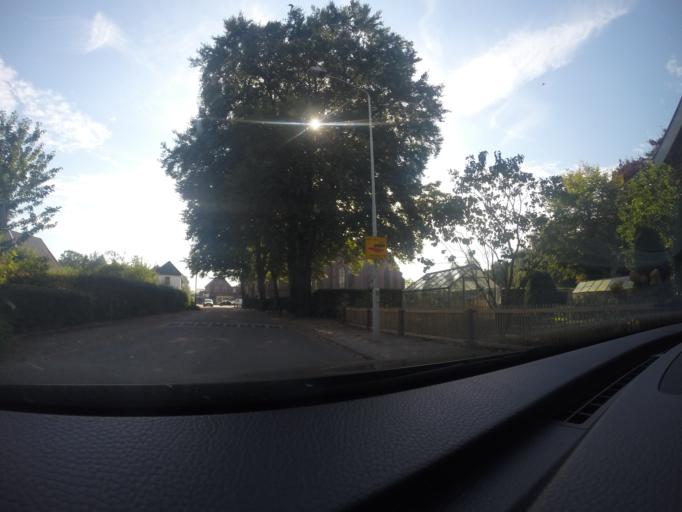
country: NL
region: Gelderland
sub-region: Gemeente Doetinchem
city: Doetinchem
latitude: 51.9399
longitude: 6.3500
